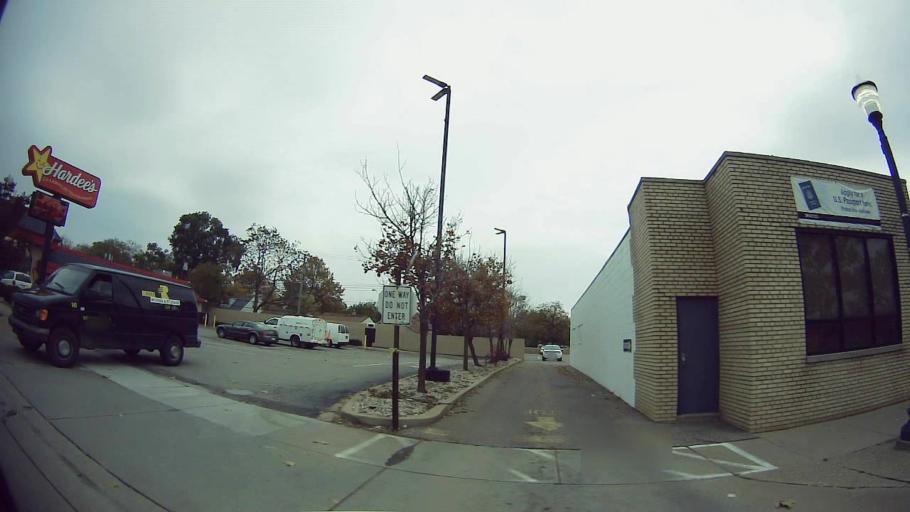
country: US
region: Michigan
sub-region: Oakland County
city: Hazel Park
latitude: 42.4629
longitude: -83.1039
